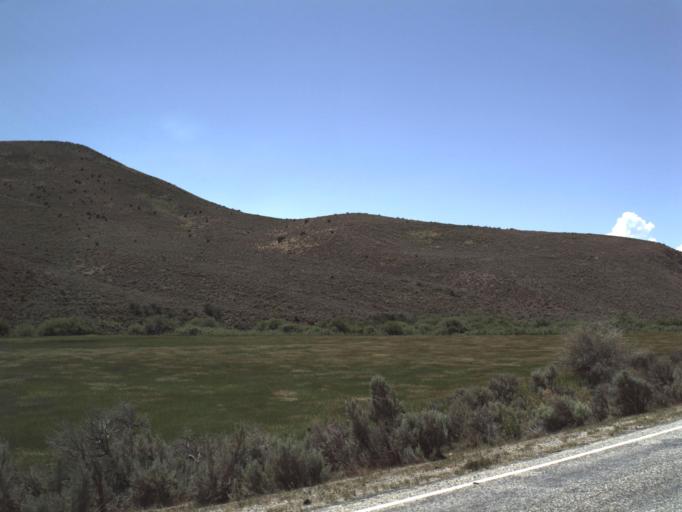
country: US
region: Utah
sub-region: Rich County
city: Randolph
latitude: 41.4990
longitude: -111.2744
